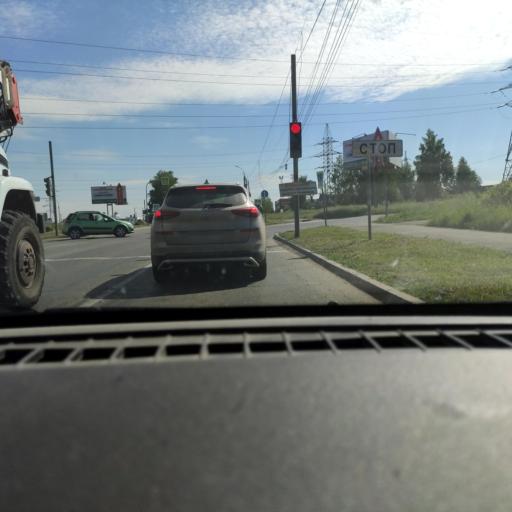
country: RU
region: Udmurtiya
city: Khokhryaki
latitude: 56.8989
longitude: 53.3090
